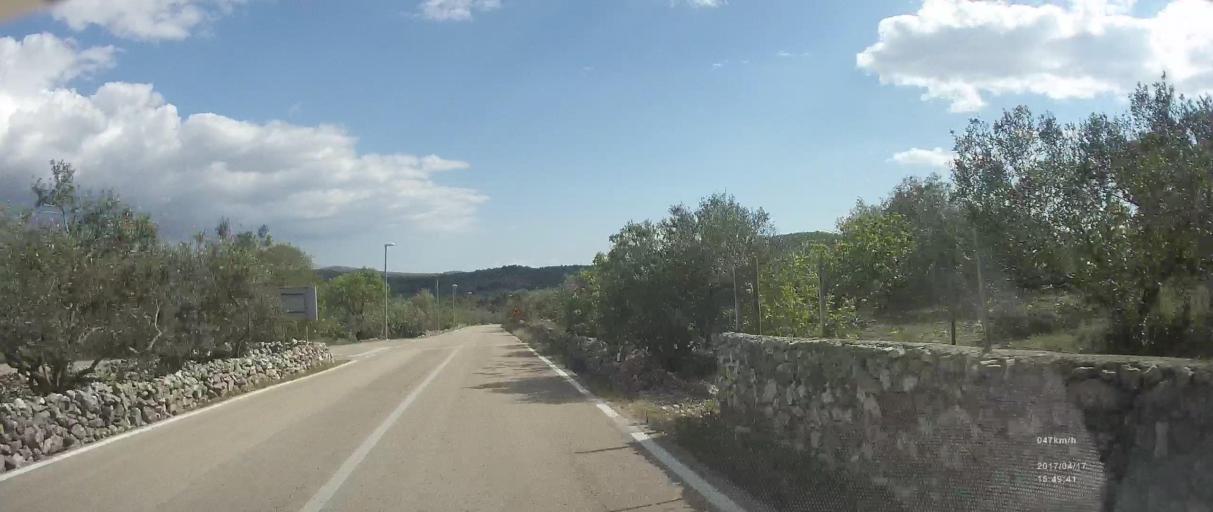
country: HR
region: Sibensko-Kniniska
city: Primosten
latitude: 43.6121
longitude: 15.9763
